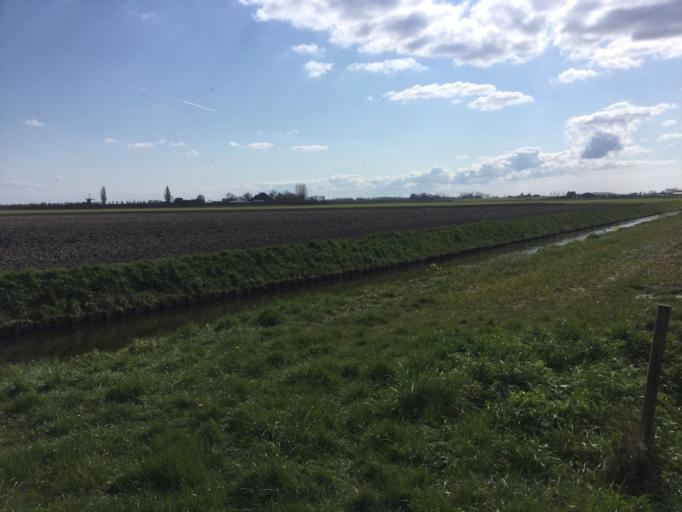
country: NL
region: South Holland
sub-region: Gemeente Lisse
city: Lisse
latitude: 52.2263
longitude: 4.5846
